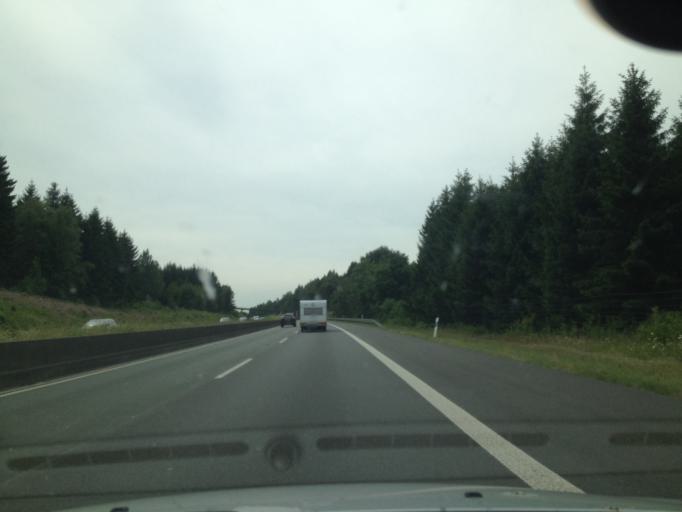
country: DE
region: North Rhine-Westphalia
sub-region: Regierungsbezirk Arnsberg
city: Drolshagen
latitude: 50.9850
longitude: 7.7980
